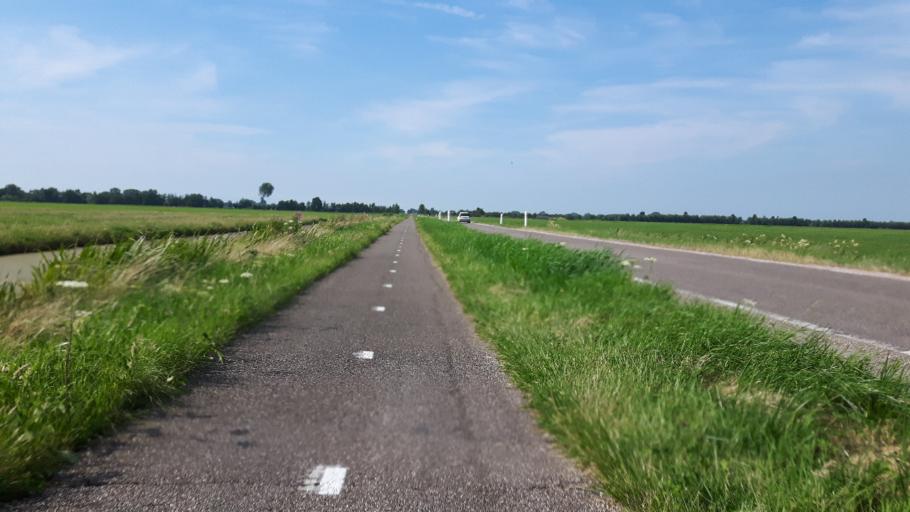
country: NL
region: Utrecht
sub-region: Gemeente Oudewater
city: Oudewater
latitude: 52.0002
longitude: 4.9002
